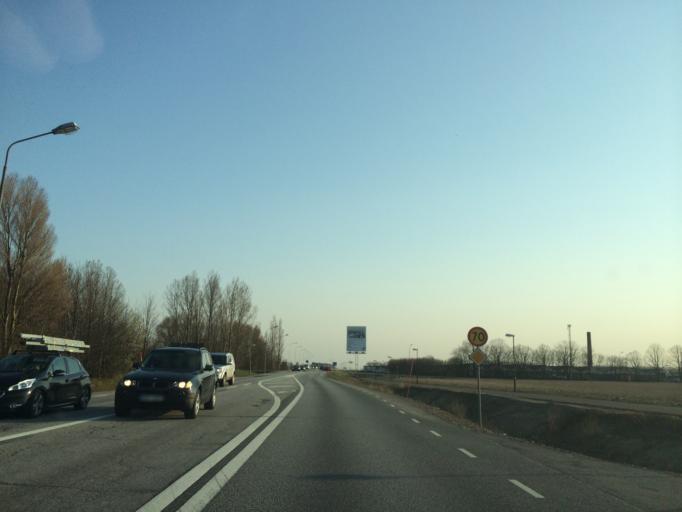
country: SE
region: Skane
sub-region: Malmo
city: Bunkeflostrand
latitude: 55.5596
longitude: 12.9838
